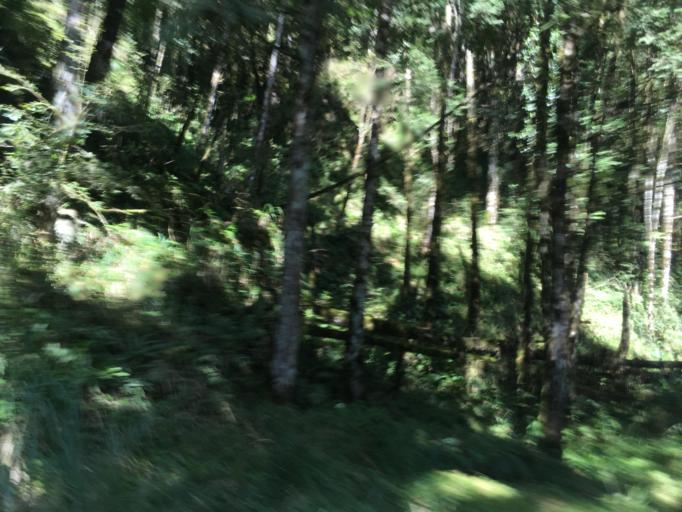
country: TW
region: Taiwan
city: Daxi
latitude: 24.6142
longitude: 121.4624
